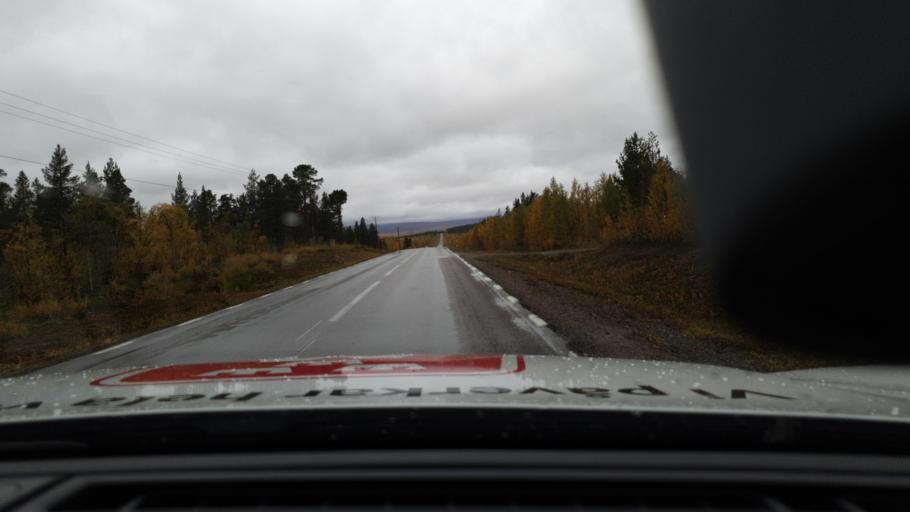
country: SE
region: Norrbotten
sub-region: Kiruna Kommun
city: Kiruna
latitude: 67.7609
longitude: 20.1026
